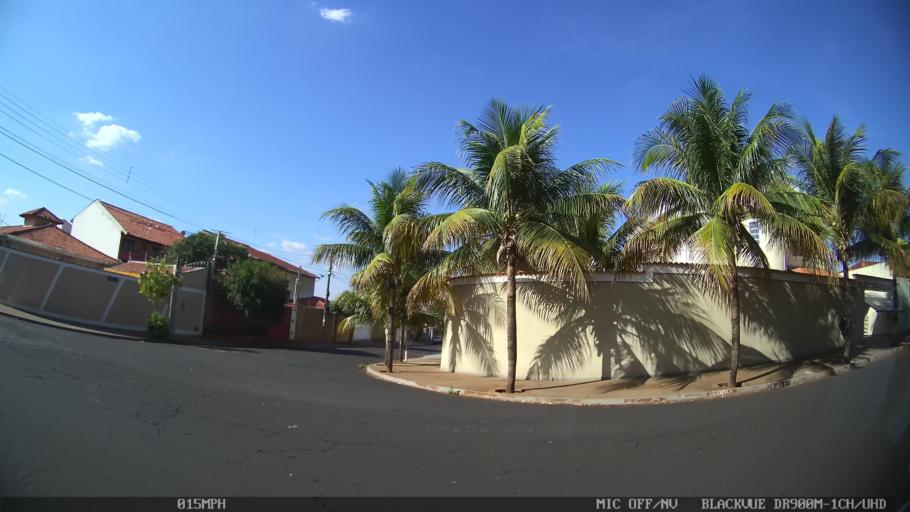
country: BR
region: Sao Paulo
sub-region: Ribeirao Preto
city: Ribeirao Preto
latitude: -21.1747
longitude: -47.7702
